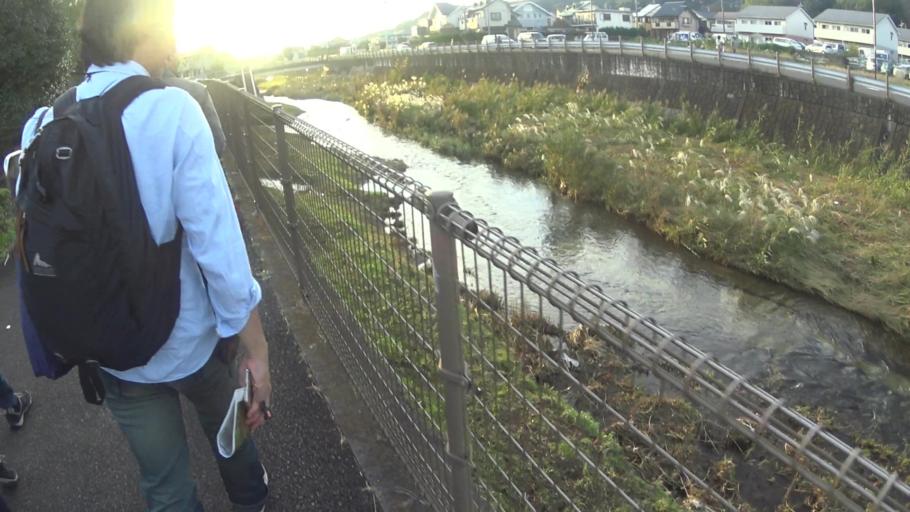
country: JP
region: Tokyo
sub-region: Machida-shi
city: Machida
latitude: 35.5865
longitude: 139.4465
